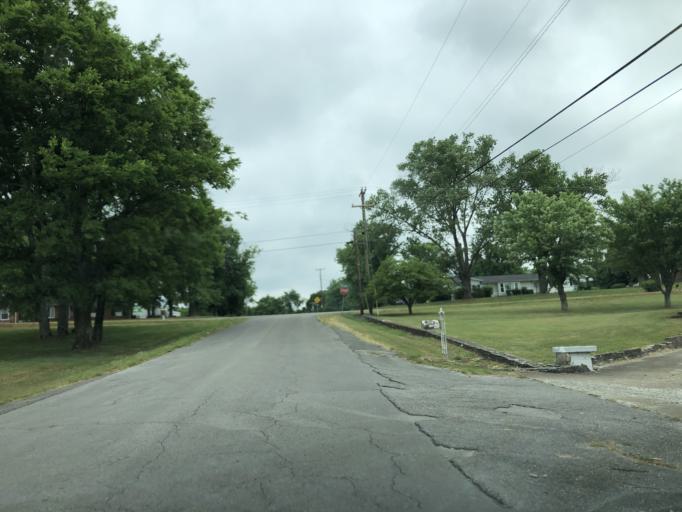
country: US
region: Tennessee
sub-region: Davidson County
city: Goodlettsville
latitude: 36.2794
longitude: -86.7590
